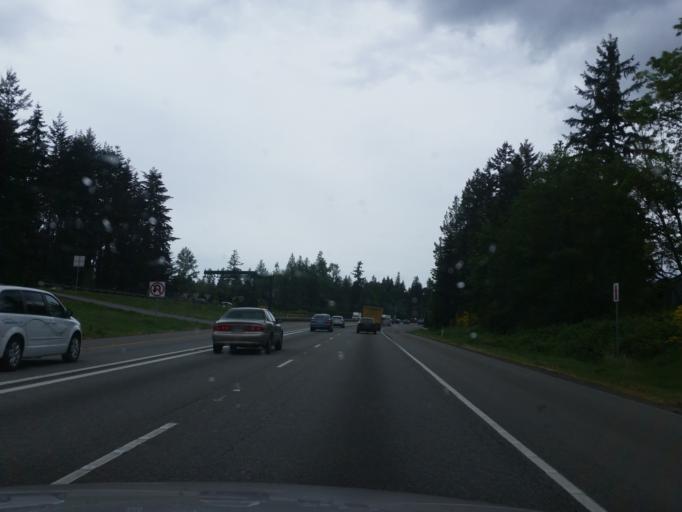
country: US
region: Washington
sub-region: Snohomish County
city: Martha Lake
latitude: 47.8163
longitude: -122.2358
